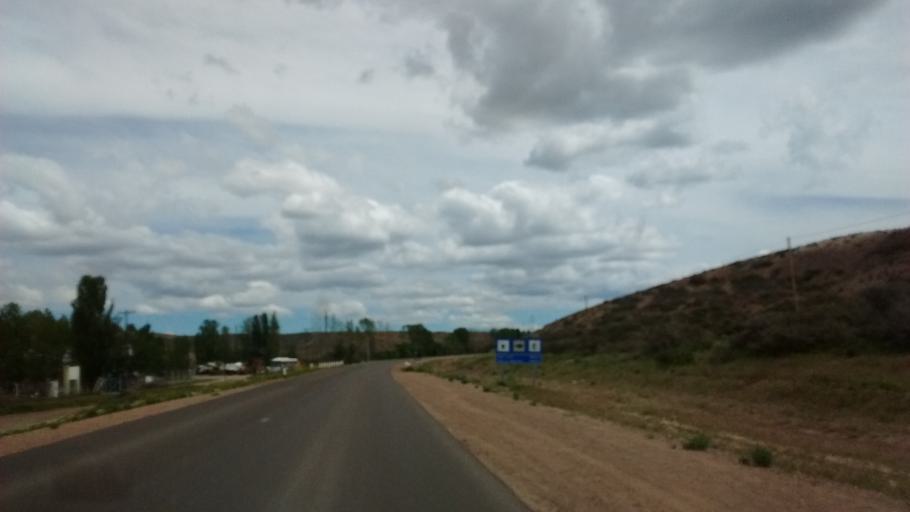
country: AR
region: Neuquen
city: Piedra del Aguila
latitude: -40.0559
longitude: -70.0854
